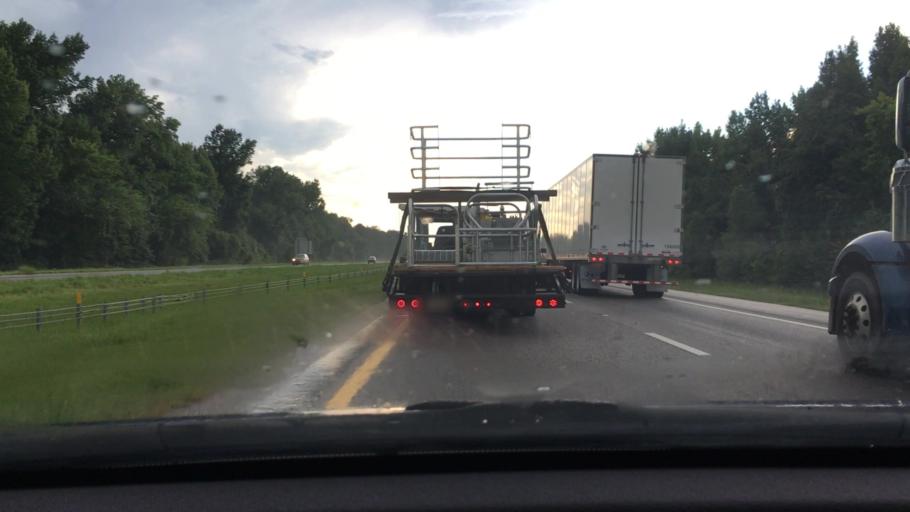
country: US
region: South Carolina
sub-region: Lee County
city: Bishopville
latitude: 34.1874
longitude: -80.2312
